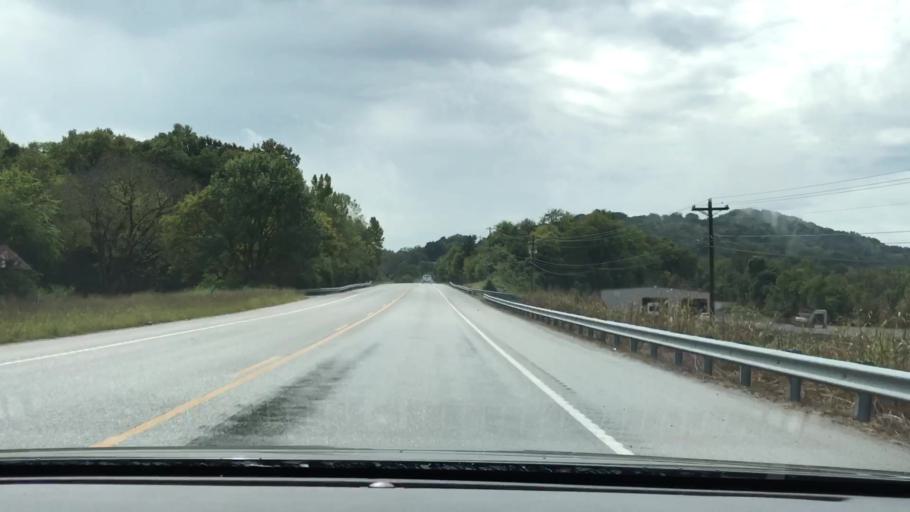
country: US
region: Tennessee
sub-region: Smith County
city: Carthage
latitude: 36.3111
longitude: -85.9723
